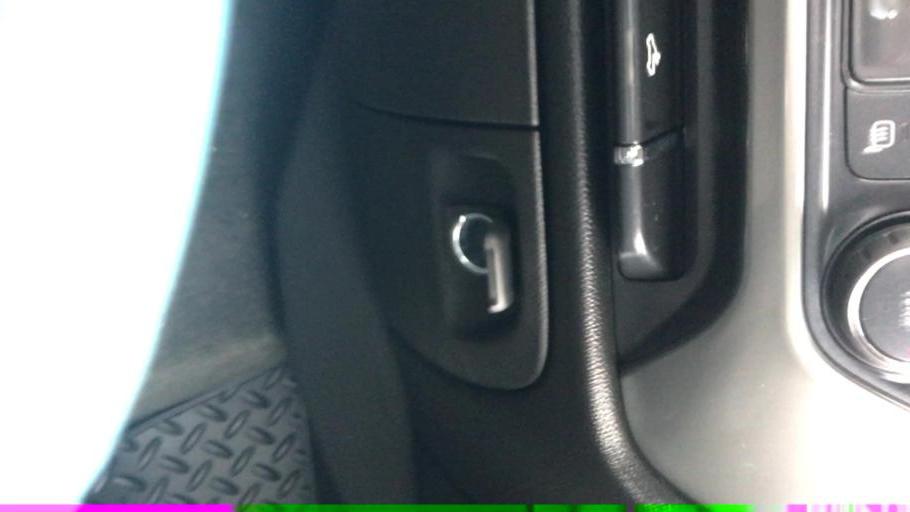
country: US
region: Texas
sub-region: Denton County
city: Flower Mound
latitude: 32.9962
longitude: -97.0647
